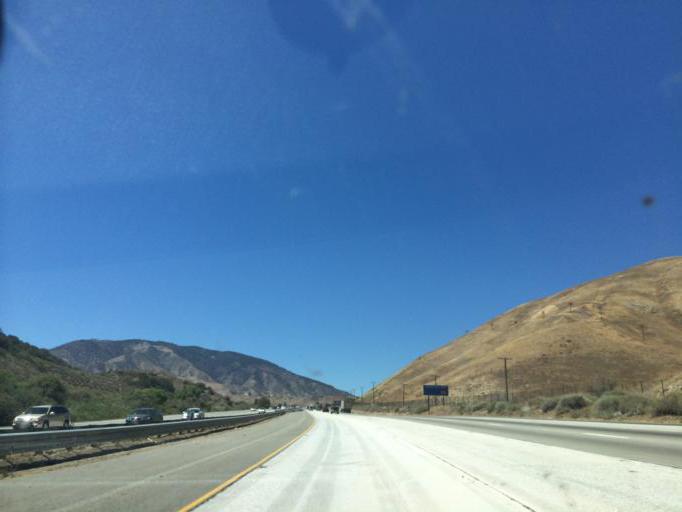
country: US
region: California
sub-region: Kern County
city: Lebec
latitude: 34.7933
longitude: -118.8380
